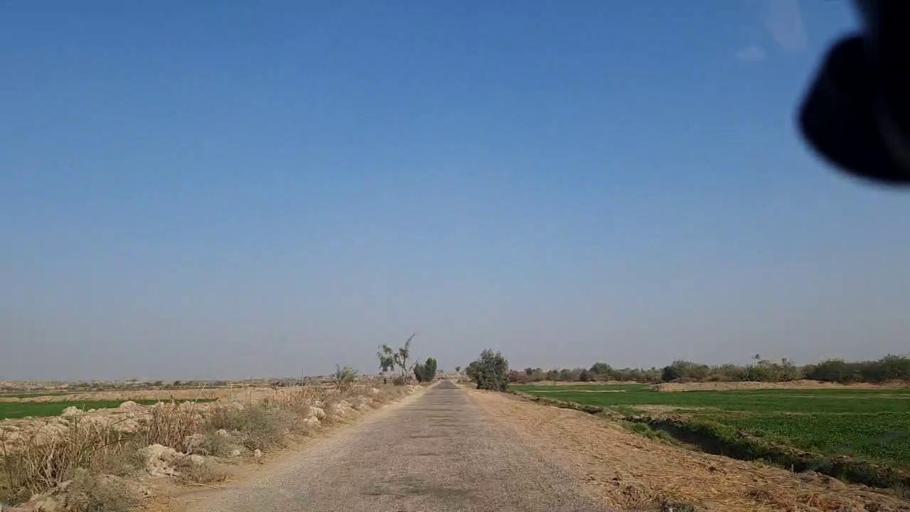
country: PK
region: Sindh
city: Khanpur
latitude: 27.6817
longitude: 69.5476
